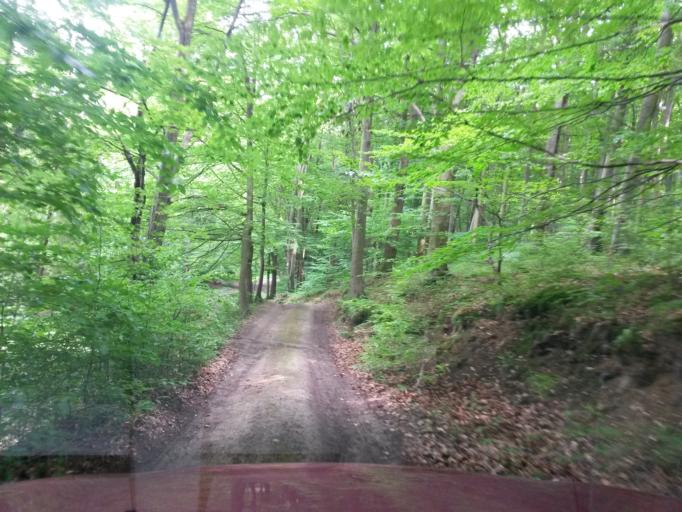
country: SK
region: Kosicky
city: Kosice
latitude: 48.7593
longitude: 21.2180
